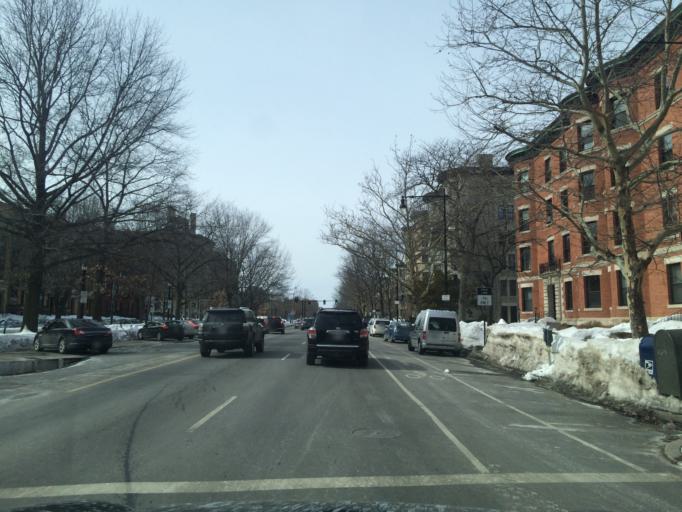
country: US
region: Massachusetts
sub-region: Norfolk County
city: Brookline
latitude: 42.3457
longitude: -71.1091
